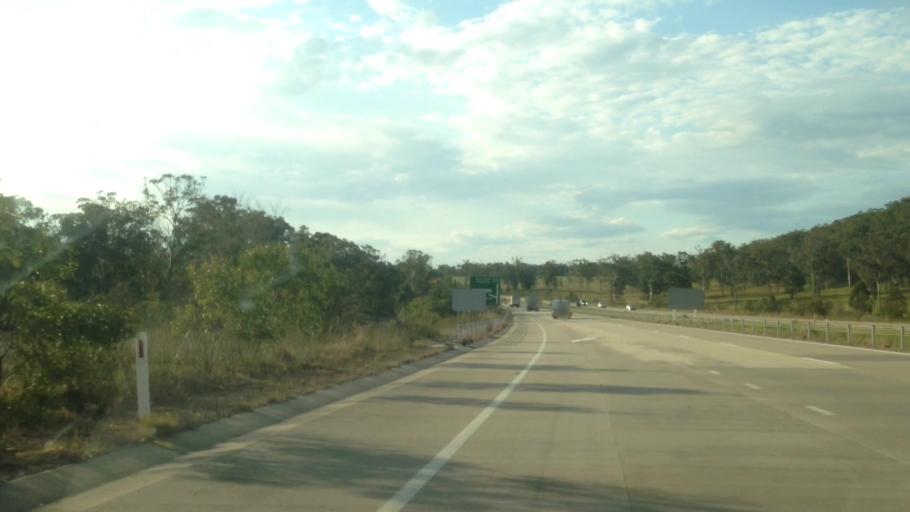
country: AU
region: New South Wales
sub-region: Cessnock
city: Heddon Greta
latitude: -32.8408
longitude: 151.5415
